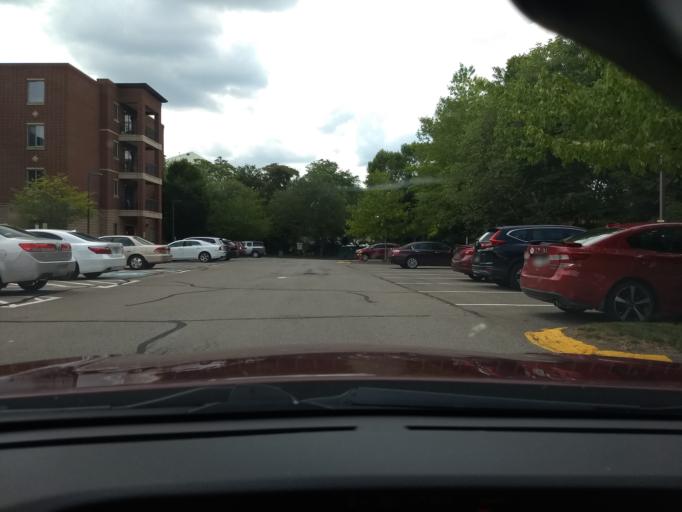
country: US
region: Pennsylvania
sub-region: Allegheny County
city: Aspinwall
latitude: 40.4862
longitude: -79.8875
